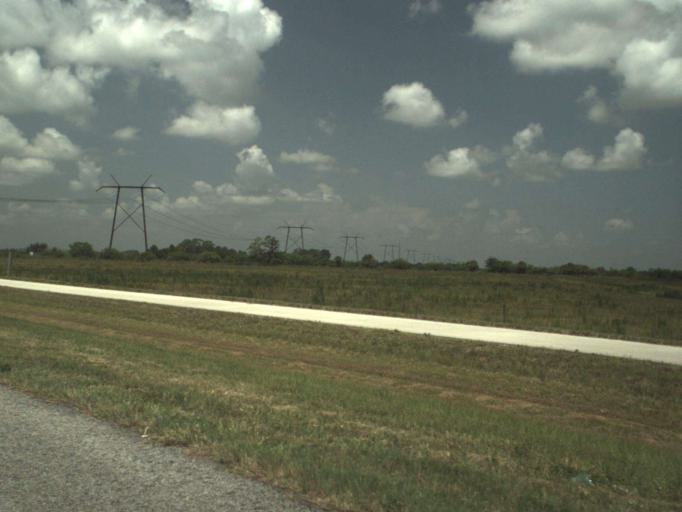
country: US
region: Florida
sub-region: Saint Lucie County
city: Fort Pierce South
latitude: 27.3836
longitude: -80.4691
